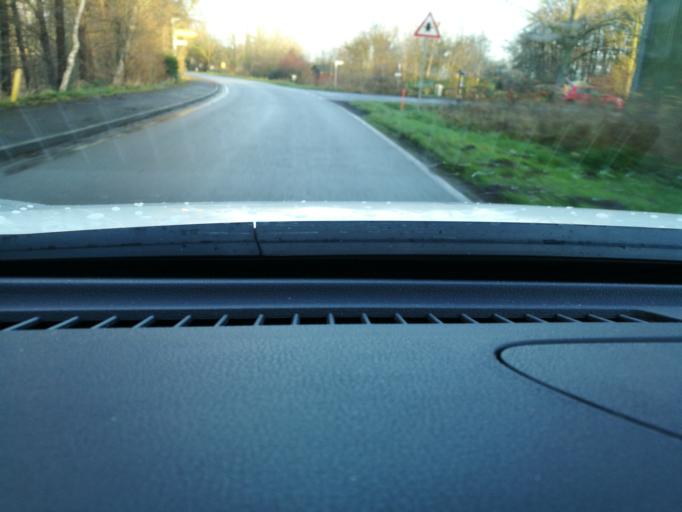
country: DE
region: Schleswig-Holstein
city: Holzbunge
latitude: 54.3962
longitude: 9.7050
